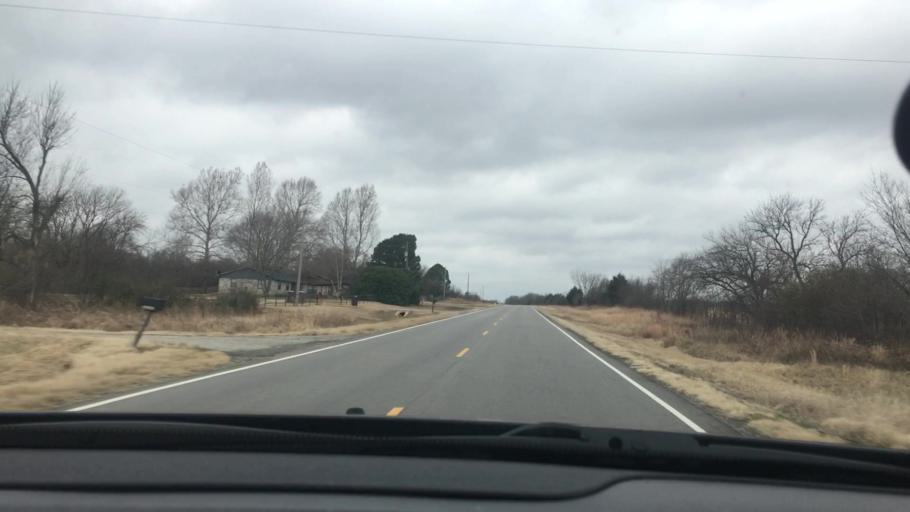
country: US
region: Oklahoma
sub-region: Atoka County
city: Atoka
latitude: 34.3749
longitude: -96.1699
